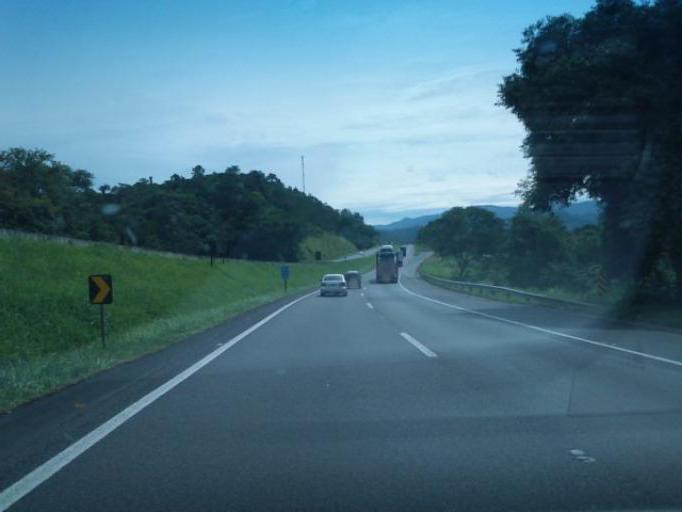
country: BR
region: Sao Paulo
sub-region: Cajati
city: Cajati
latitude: -24.7496
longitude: -48.1515
